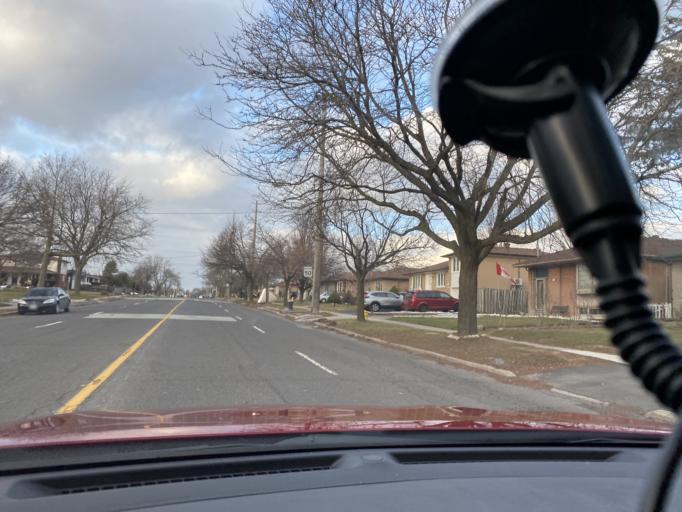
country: CA
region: Ontario
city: Scarborough
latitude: 43.7739
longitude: -79.2203
